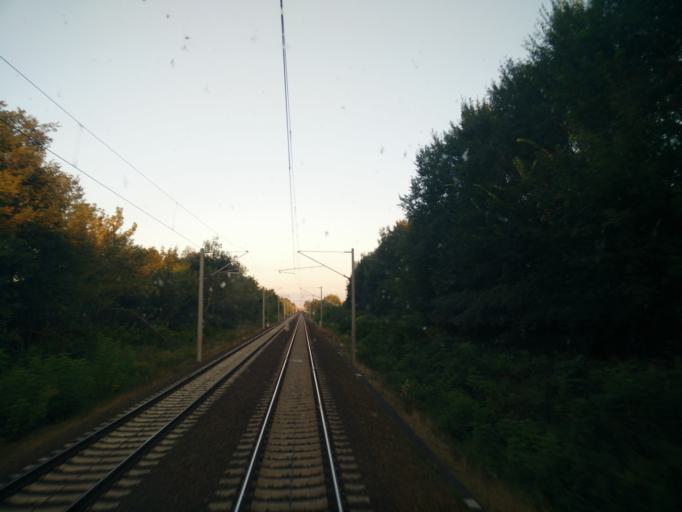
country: DE
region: Brandenburg
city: Dallgow-Doeberitz
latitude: 52.5654
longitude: 13.0678
